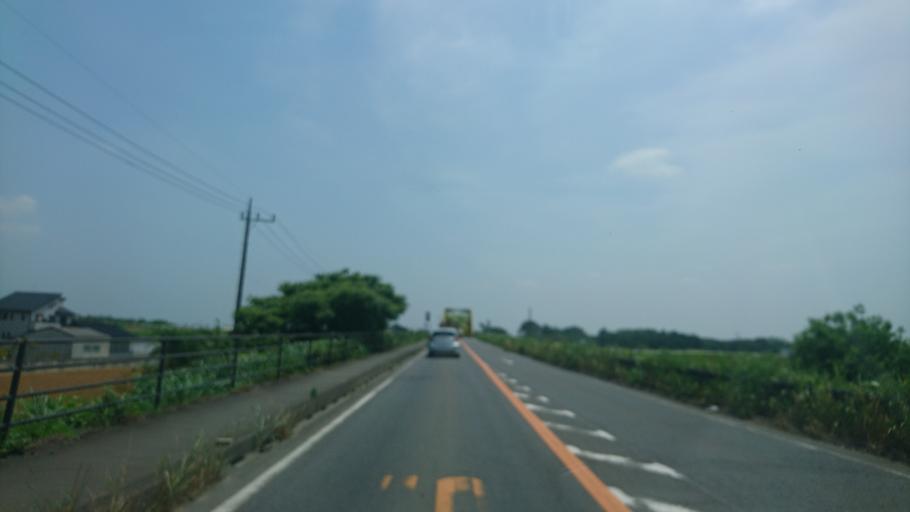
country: JP
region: Ibaraki
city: Mitsukaido
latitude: 36.0643
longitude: 139.9749
